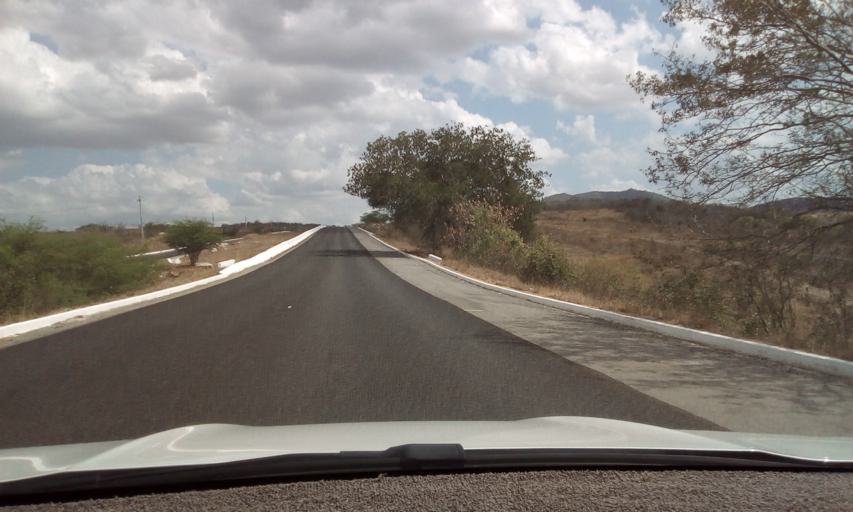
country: BR
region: Pernambuco
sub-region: Toritama
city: Toritama
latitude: -8.0579
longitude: -36.0483
